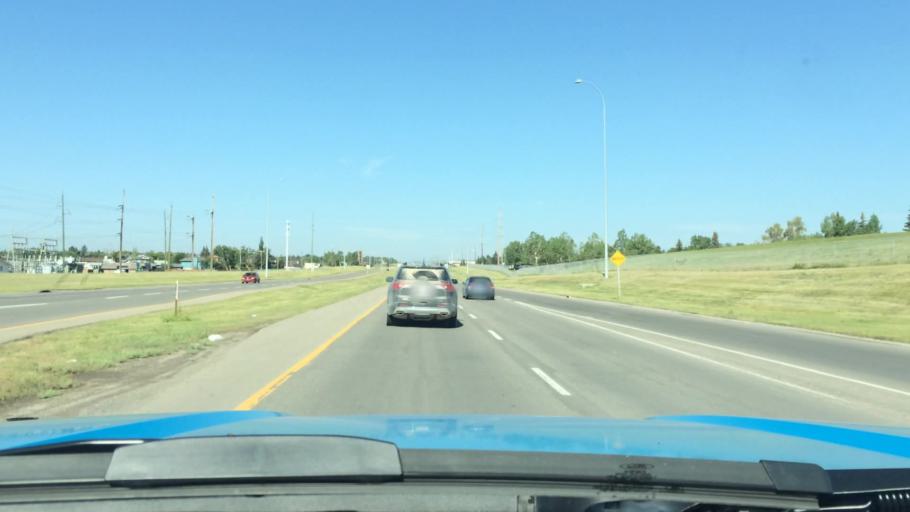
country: CA
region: Alberta
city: Chestermere
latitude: 51.0962
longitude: -113.9364
